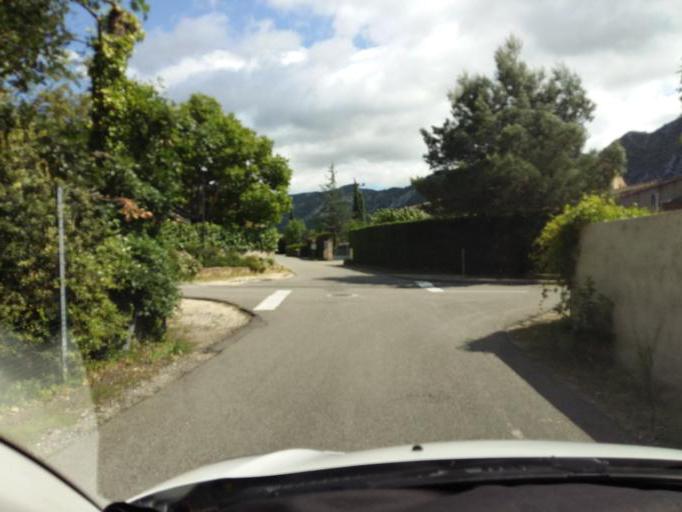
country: FR
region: Provence-Alpes-Cote d'Azur
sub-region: Departement du Vaucluse
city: Maubec
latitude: 43.8441
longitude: 5.1366
